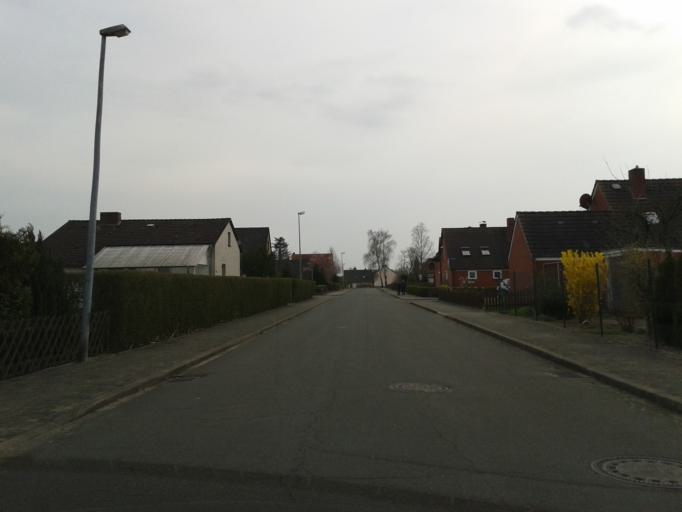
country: DE
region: Lower Saxony
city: Wustrow
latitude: 52.9269
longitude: 11.1290
